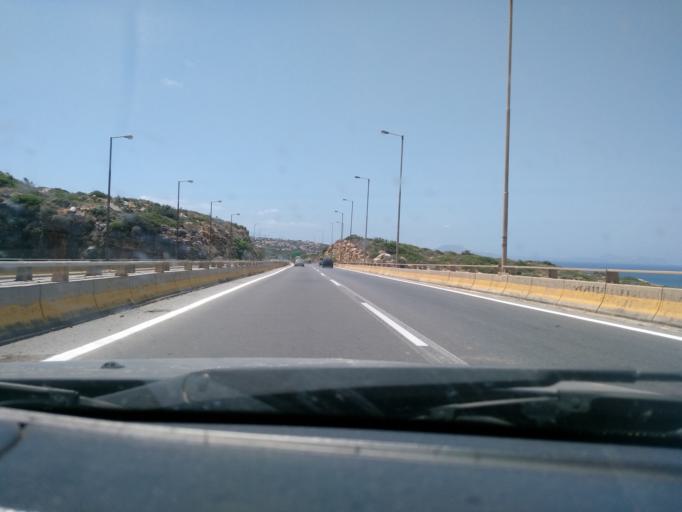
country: GR
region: Crete
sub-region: Nomos Rethymnis
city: Rethymno
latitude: 35.3583
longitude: 24.4602
